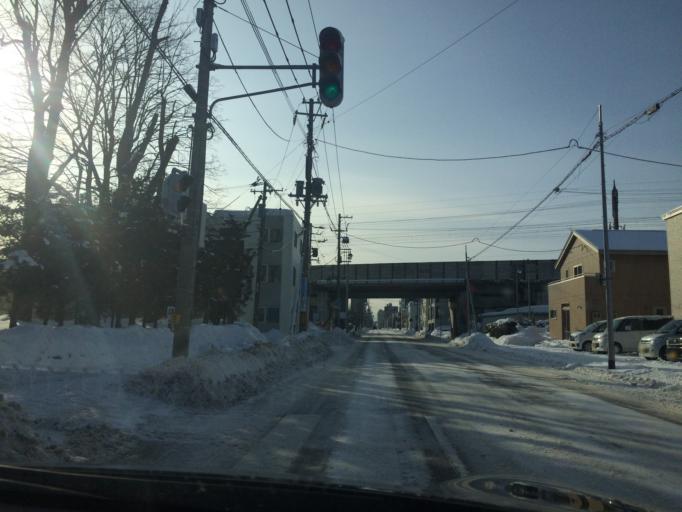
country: JP
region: Hokkaido
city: Ebetsu
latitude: 43.0421
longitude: 141.4618
